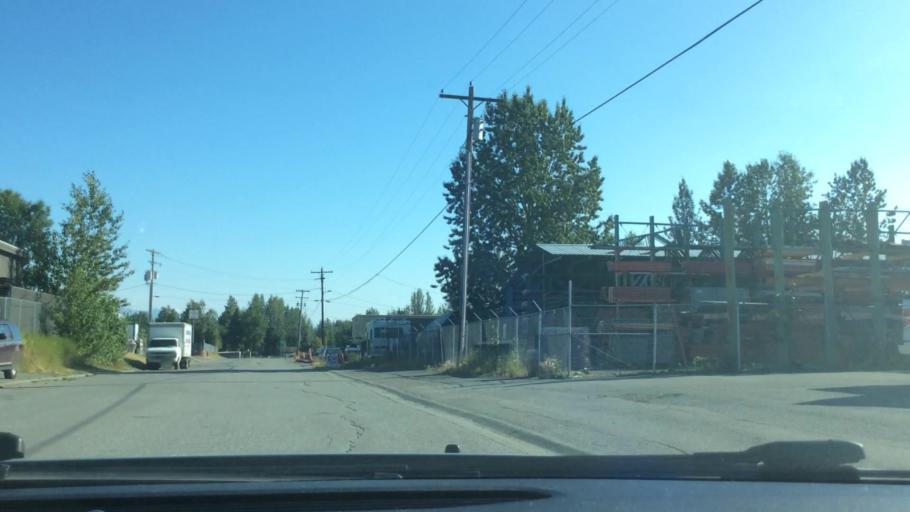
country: US
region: Alaska
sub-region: Anchorage Municipality
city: Anchorage
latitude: 61.1649
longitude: -149.8460
